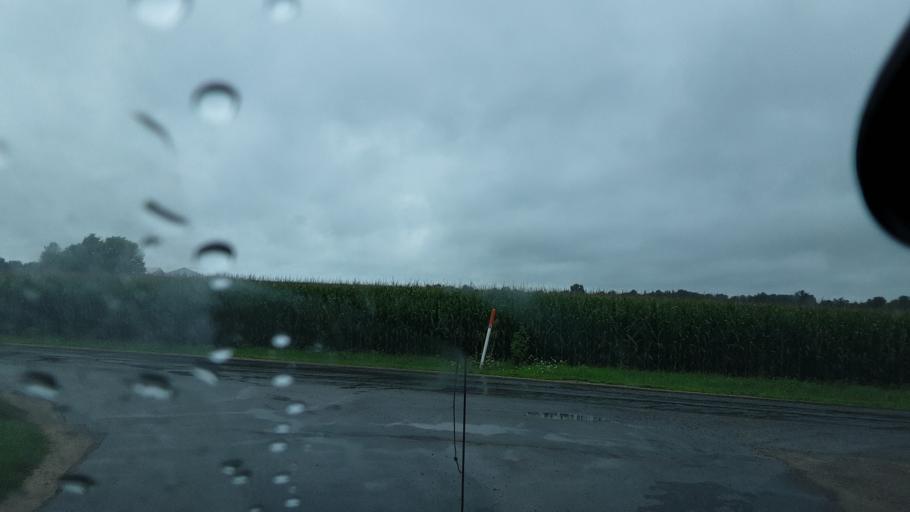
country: US
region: Indiana
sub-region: Adams County
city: Decatur
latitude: 40.7608
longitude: -84.8577
